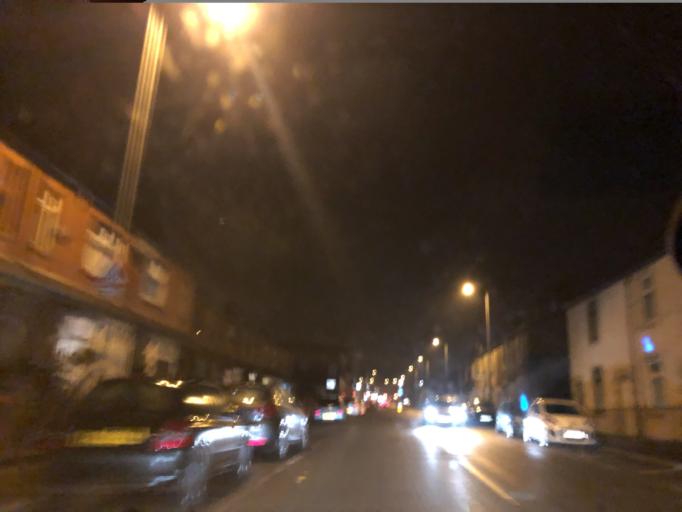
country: GB
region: England
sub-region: Borough of Oldham
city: Shaw
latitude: 53.5608
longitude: -2.0774
